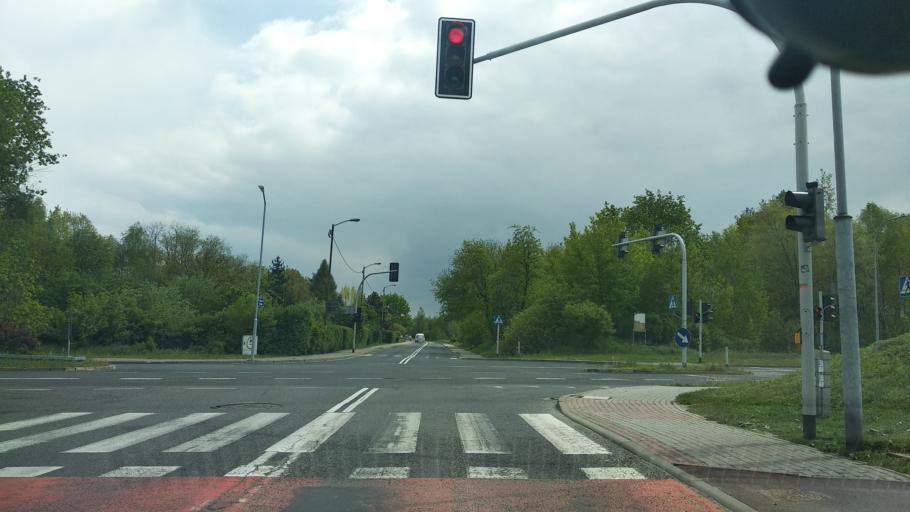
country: PL
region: Silesian Voivodeship
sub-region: Chorzow
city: Chorzow
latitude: 50.2602
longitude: 18.9796
